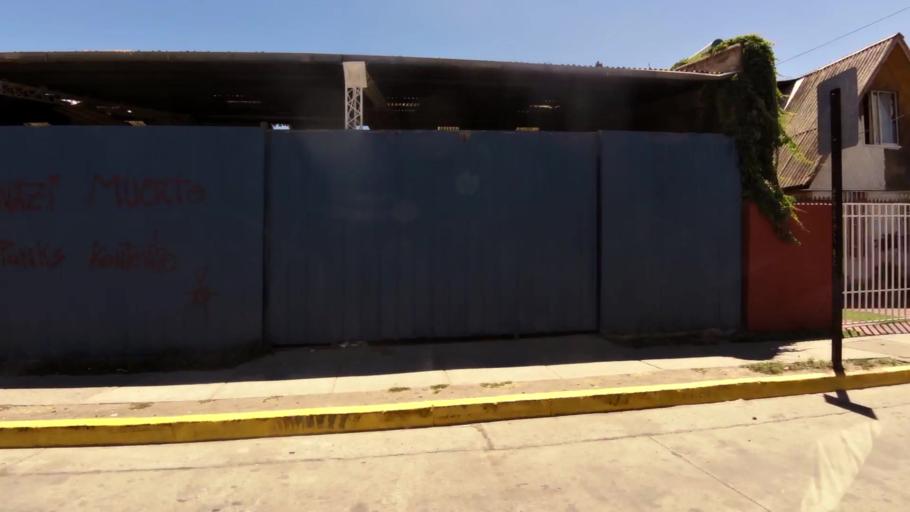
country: CL
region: O'Higgins
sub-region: Provincia de Cachapoal
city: Rancagua
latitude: -34.1659
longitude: -70.7647
